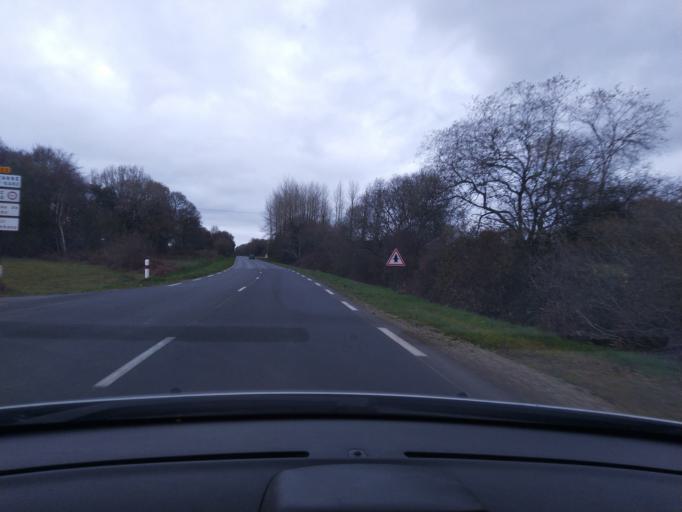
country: FR
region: Brittany
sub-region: Departement des Cotes-d'Armor
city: Plouaret
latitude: 48.5822
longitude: -3.4945
